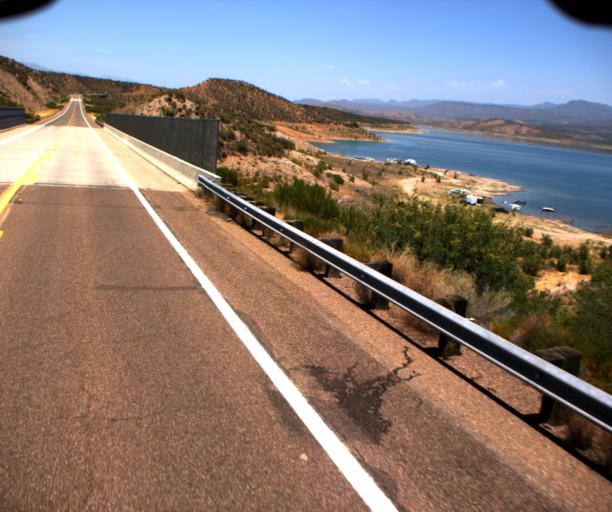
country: US
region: Arizona
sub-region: Gila County
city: Tonto Basin
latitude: 33.7094
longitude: -111.1985
